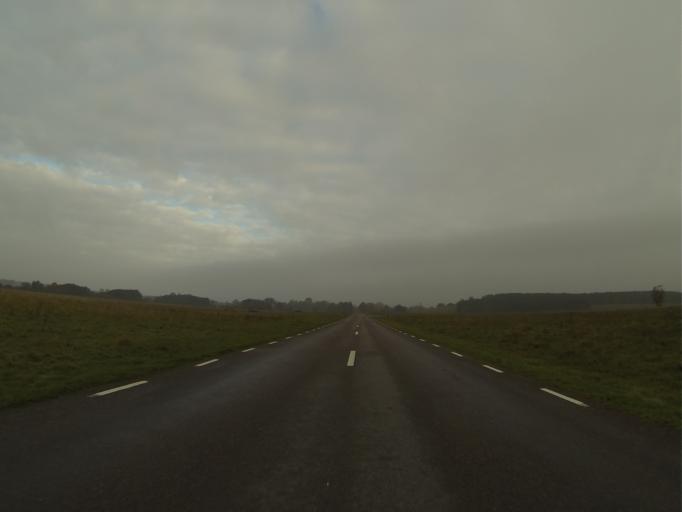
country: SE
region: Skane
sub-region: Lunds Kommun
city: Veberod
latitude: 55.6757
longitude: 13.4988
